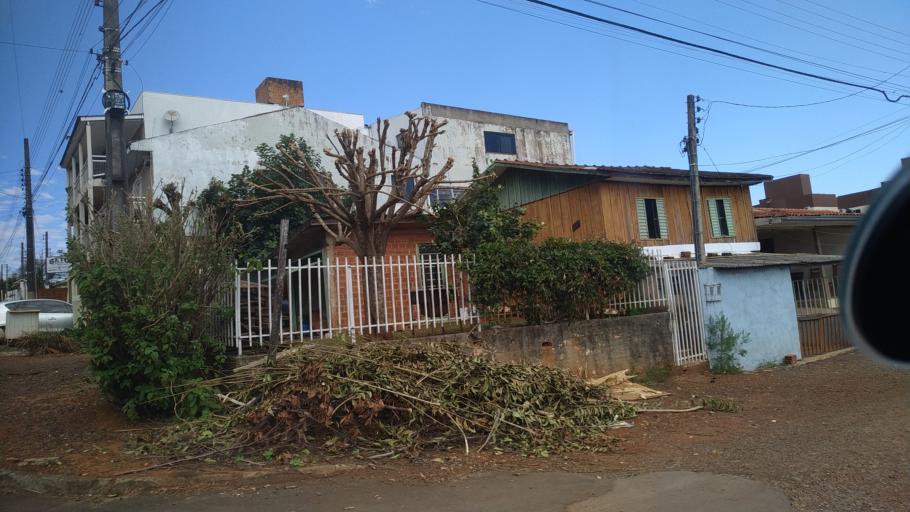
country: BR
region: Santa Catarina
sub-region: Chapeco
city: Chapeco
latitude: -27.1182
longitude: -52.6242
